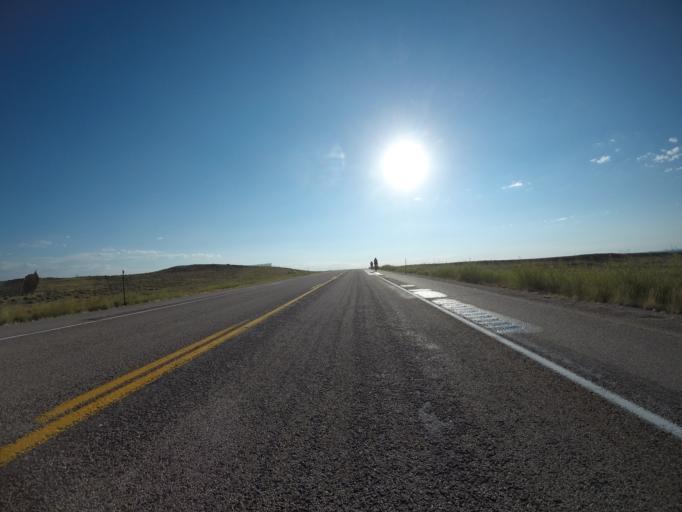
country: US
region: Wyoming
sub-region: Lincoln County
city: Kemmerer
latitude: 41.8885
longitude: -110.3621
